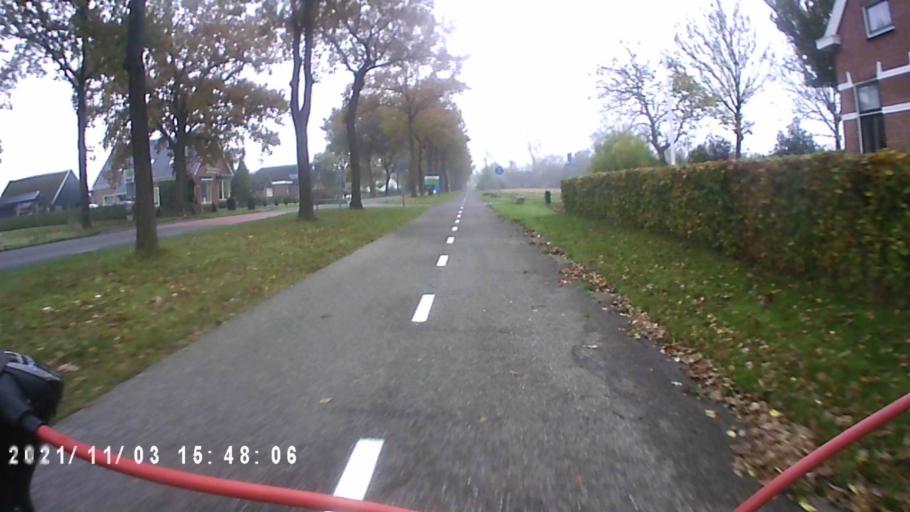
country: NL
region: Groningen
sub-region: Gemeente Leek
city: Leek
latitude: 53.0885
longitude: 6.3394
